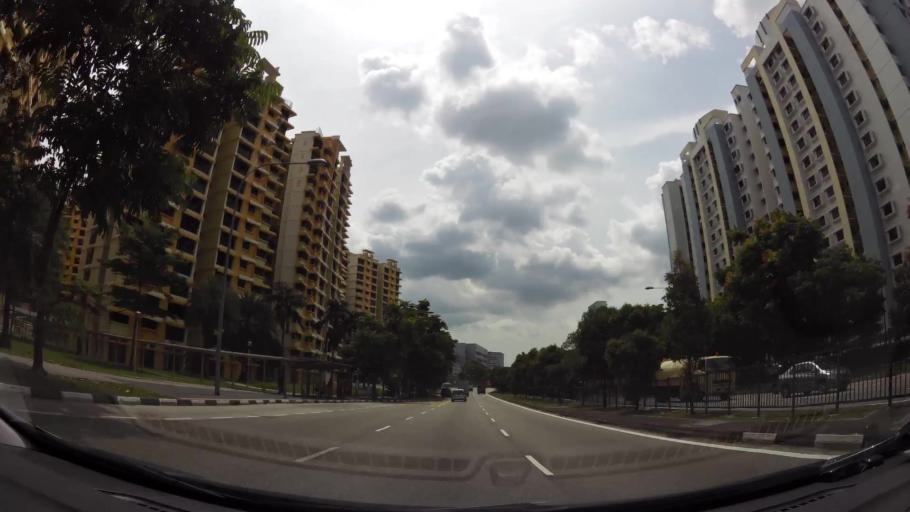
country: MY
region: Johor
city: Johor Bahru
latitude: 1.3367
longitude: 103.6962
